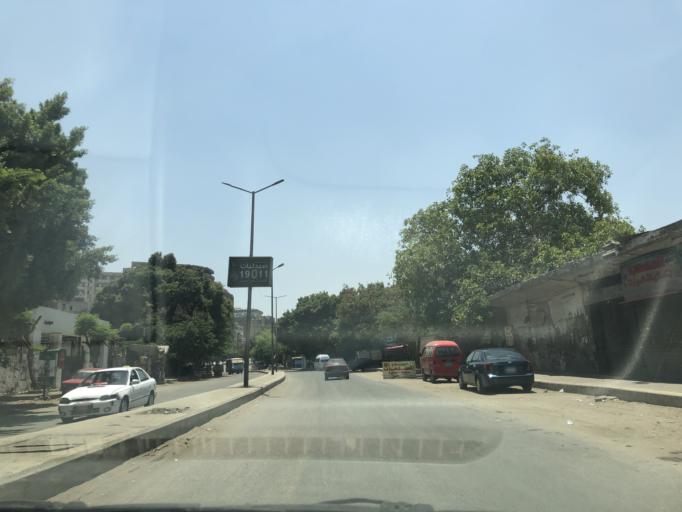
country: EG
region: Muhafazat al Qahirah
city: Cairo
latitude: 30.0669
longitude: 31.2709
